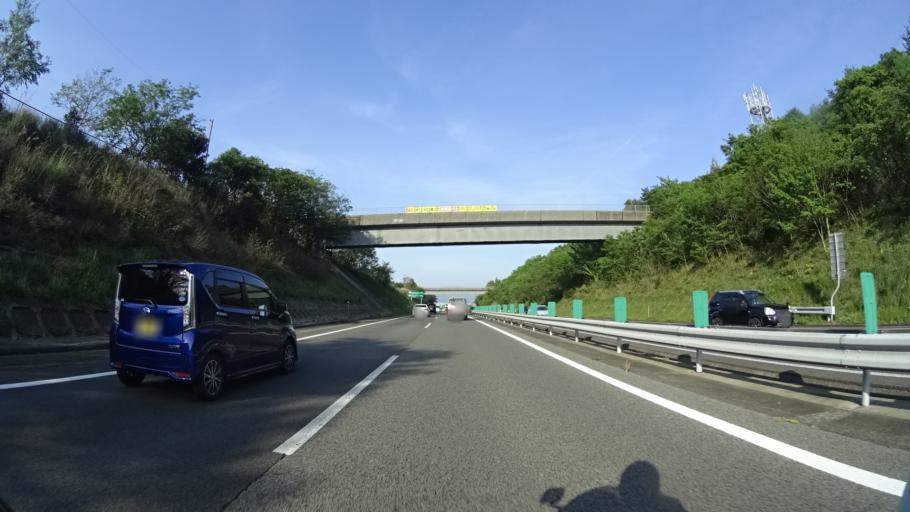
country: JP
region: Ehime
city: Kawanoecho
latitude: 33.9569
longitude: 133.4742
